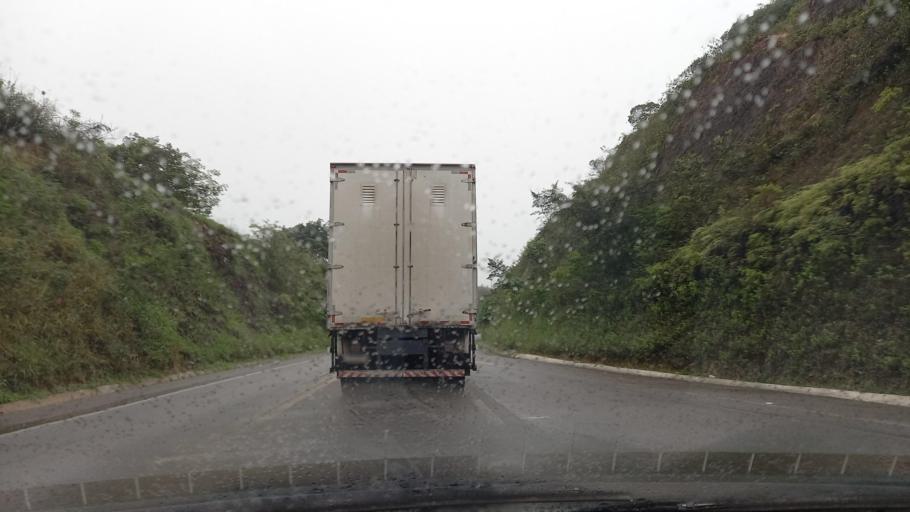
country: BR
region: Pernambuco
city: Garanhuns
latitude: -8.8778
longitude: -36.5104
